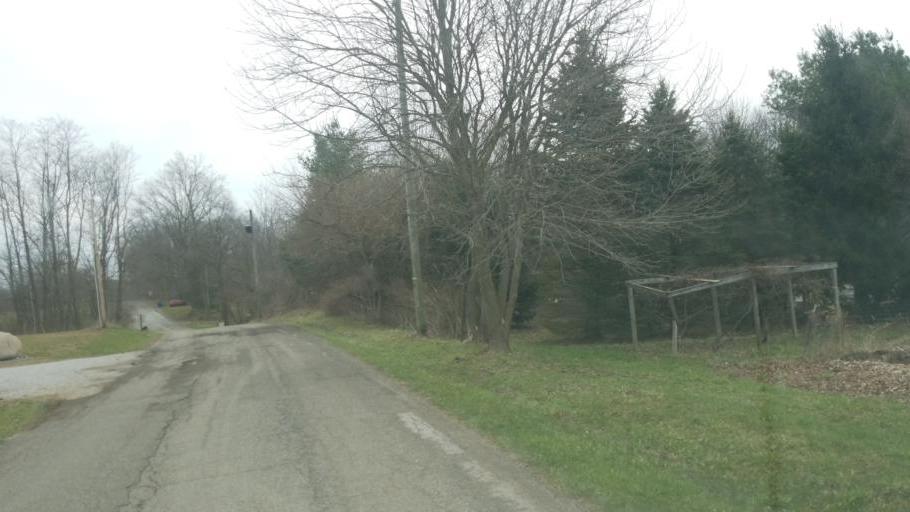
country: US
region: Ohio
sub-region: Knox County
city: Centerburg
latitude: 40.3535
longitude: -82.6372
